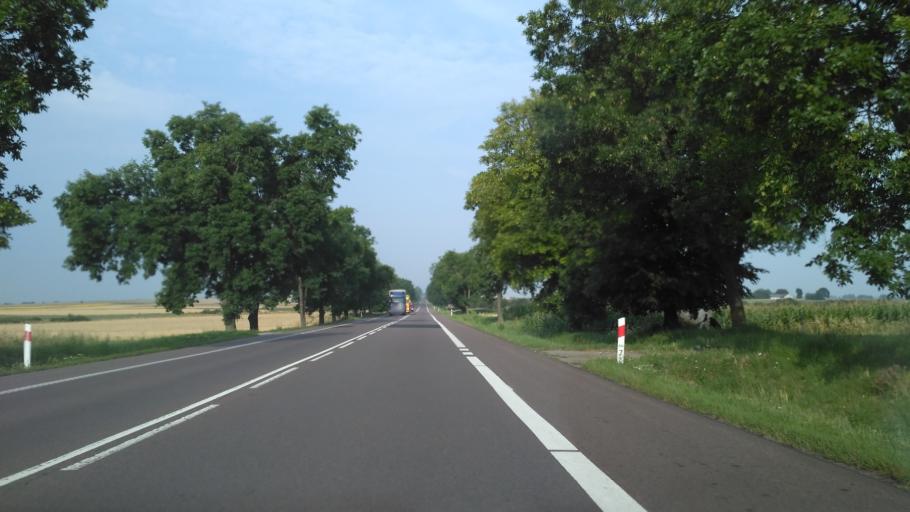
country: PL
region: Lublin Voivodeship
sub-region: Powiat chelmski
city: Rejowiec Fabryczny
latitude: 51.1724
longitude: 23.1363
